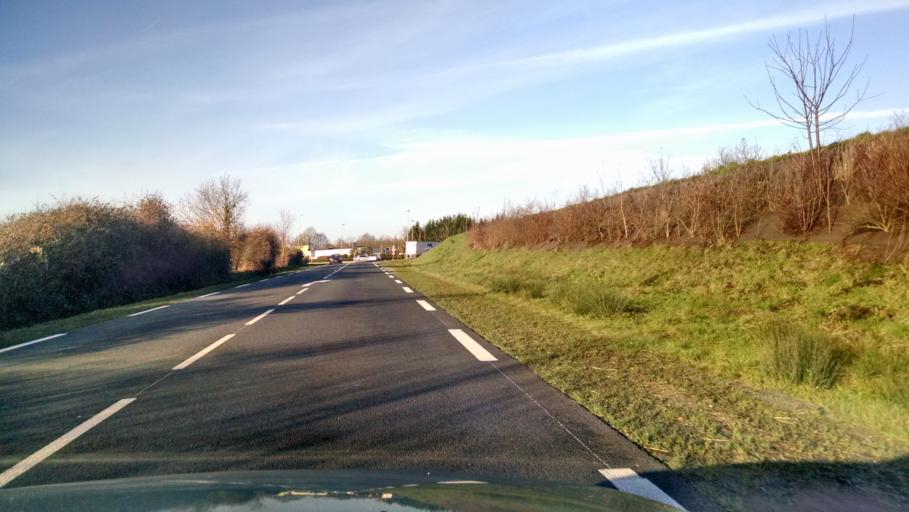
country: FR
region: Pays de la Loire
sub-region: Departement de la Vendee
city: Bouffere
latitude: 46.9726
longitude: -1.3306
